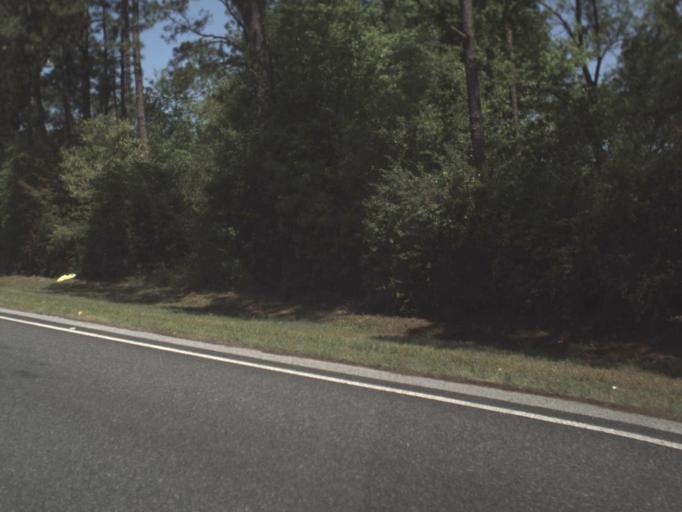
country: US
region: Florida
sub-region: Escambia County
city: Ensley
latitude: 30.5321
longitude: -87.3306
